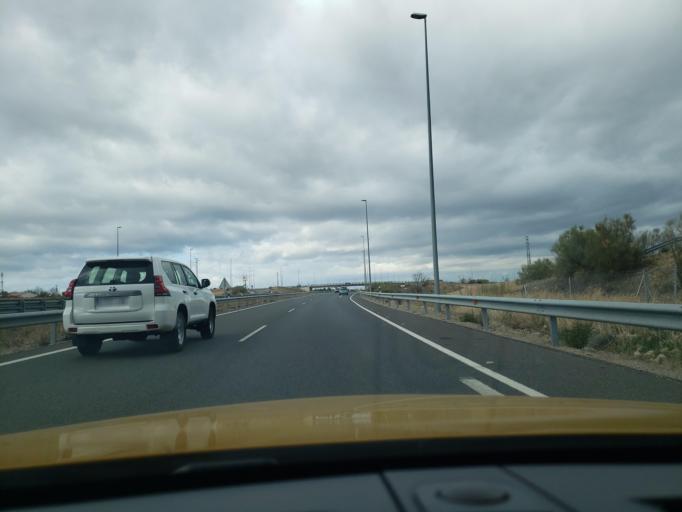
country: ES
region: Andalusia
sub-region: Provincia de Jaen
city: Jaen
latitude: 37.8118
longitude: -3.7647
